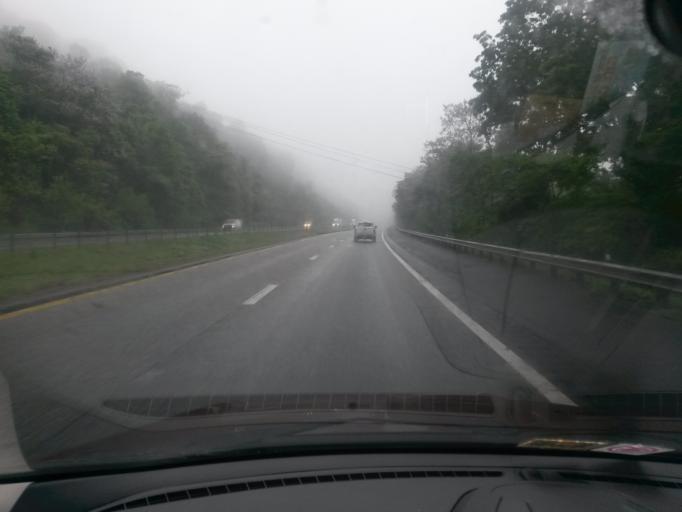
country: US
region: Virginia
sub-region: City of Waynesboro
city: Waynesboro
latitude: 38.0383
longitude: -78.8377
